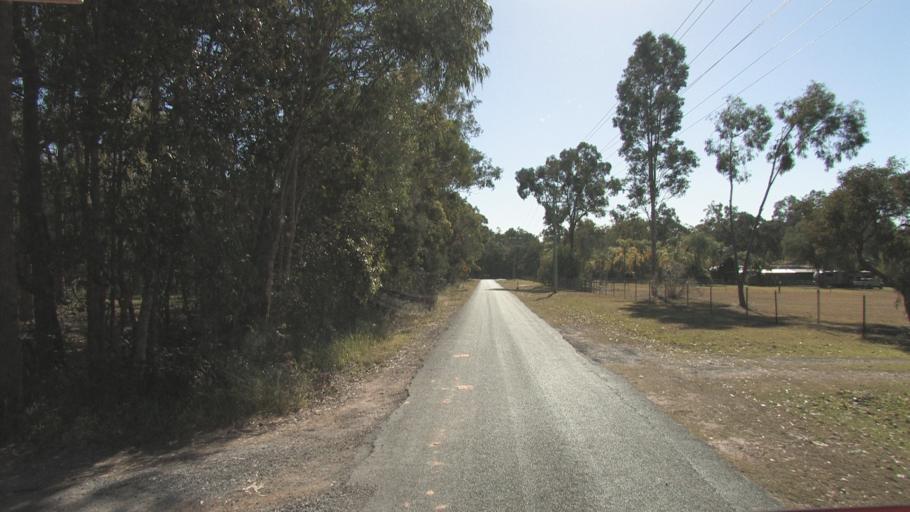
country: AU
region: Queensland
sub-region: Logan
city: Park Ridge South
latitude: -27.7487
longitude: 153.0483
